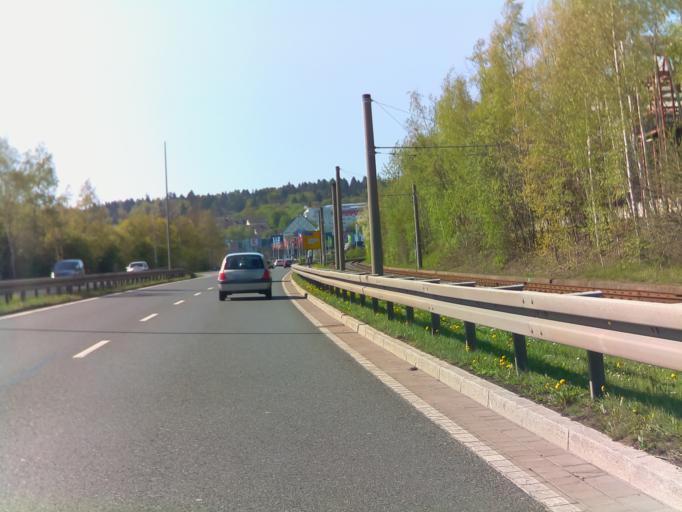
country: DE
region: Saxony
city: Plauen
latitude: 50.5009
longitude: 12.1710
